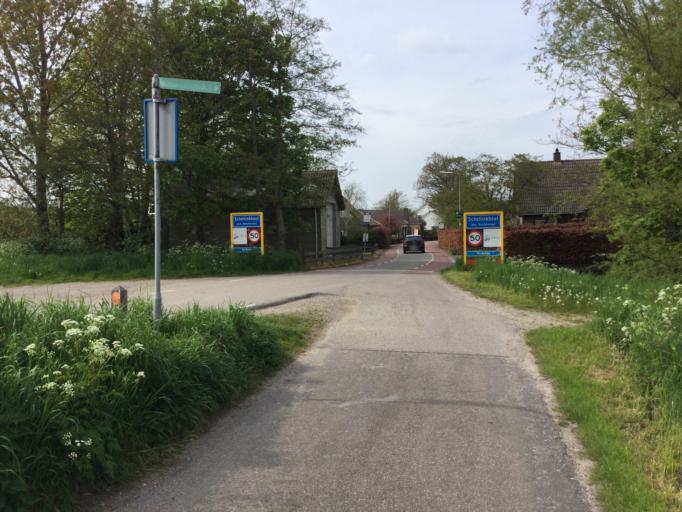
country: NL
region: North Holland
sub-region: Gemeente Hoorn
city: Hoorn
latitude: 52.6273
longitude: 5.1279
